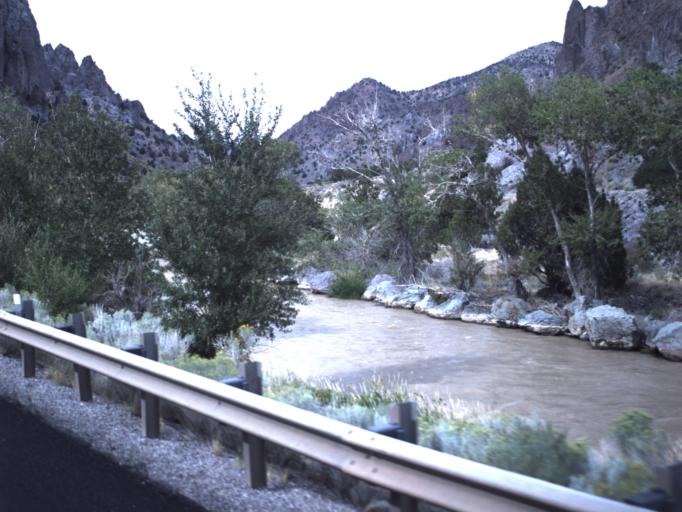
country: US
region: Utah
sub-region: Sevier County
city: Monroe
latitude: 38.5408
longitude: -112.2685
